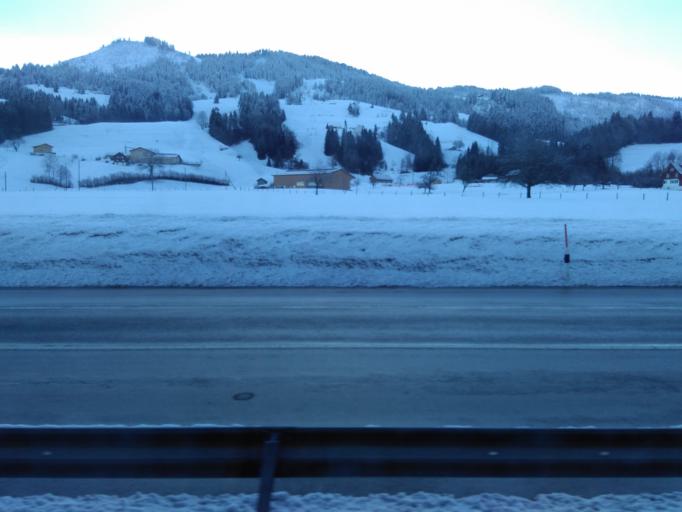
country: CH
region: Schwyz
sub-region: Bezirk Schwyz
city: Rothenthurm
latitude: 47.0936
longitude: 8.6695
